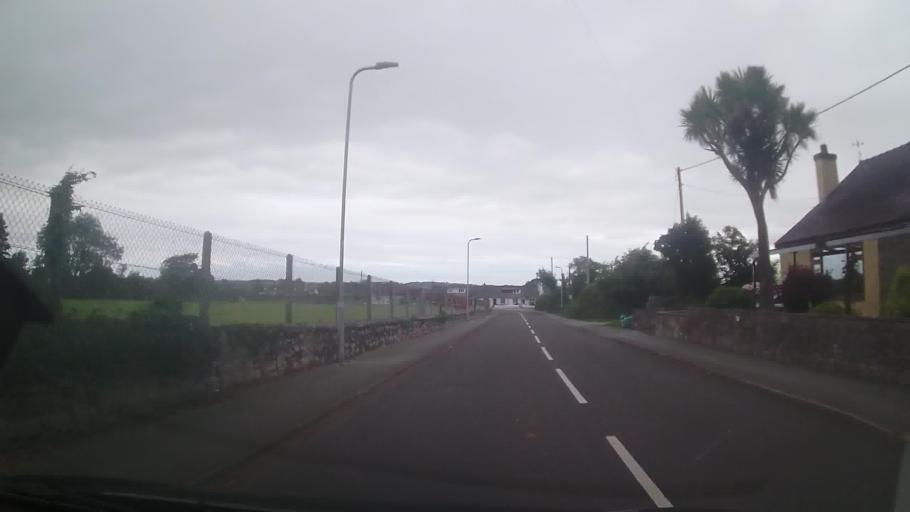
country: GB
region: Wales
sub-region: Gwynedd
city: Caernarfon
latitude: 53.1804
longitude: -4.2762
